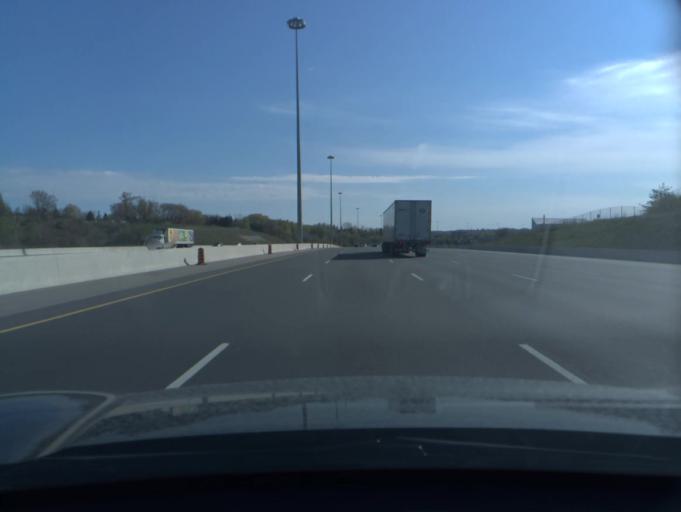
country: CA
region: Ontario
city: North Perth
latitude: 43.8179
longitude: -80.9998
